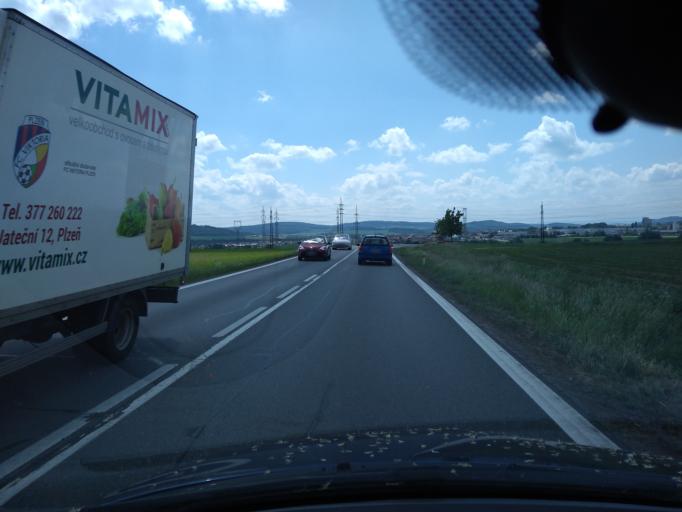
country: CZ
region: Plzensky
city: Prestice
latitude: 49.5939
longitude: 13.3273
